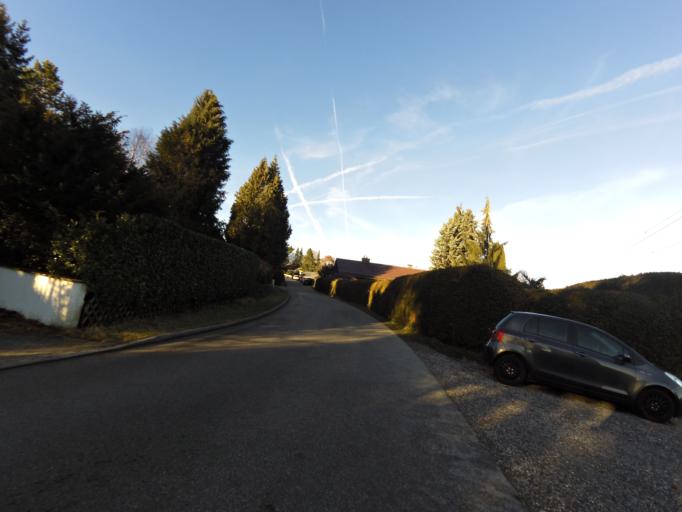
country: DE
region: Bavaria
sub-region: Upper Bavaria
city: Icking
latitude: 47.9580
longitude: 11.4394
